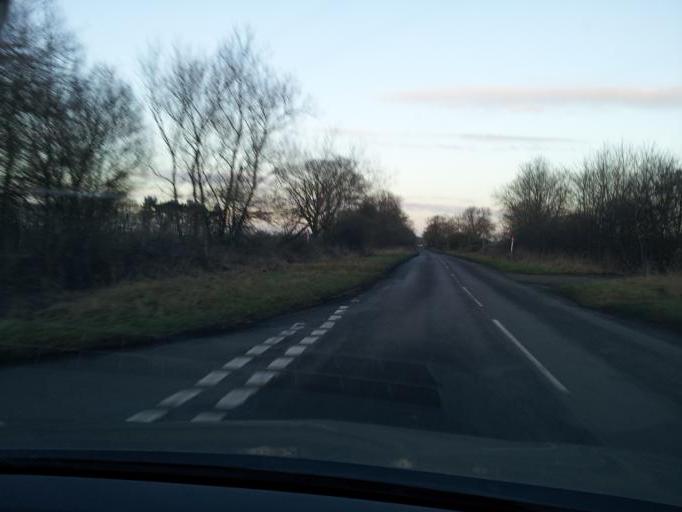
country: GB
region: England
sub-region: Leicestershire
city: Houghton on the Hill
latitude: 52.6075
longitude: -1.0193
